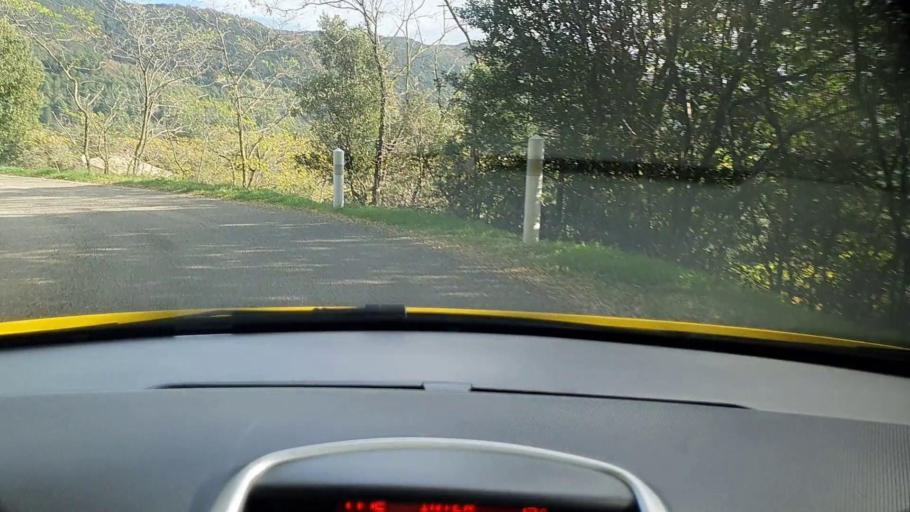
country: FR
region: Languedoc-Roussillon
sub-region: Departement du Gard
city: Lasalle
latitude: 44.0620
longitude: 3.8295
